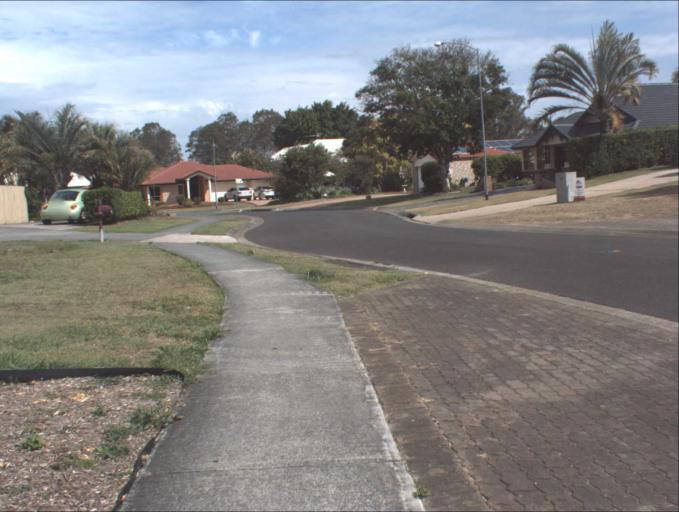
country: AU
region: Queensland
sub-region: Logan
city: Beenleigh
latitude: -27.6779
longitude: 153.2072
